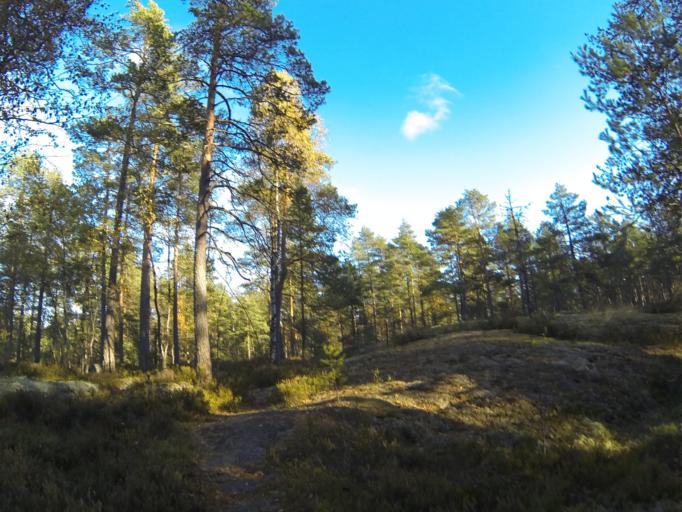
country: FI
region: Varsinais-Suomi
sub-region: Salo
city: Saerkisalo
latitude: 60.2111
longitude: 22.9285
